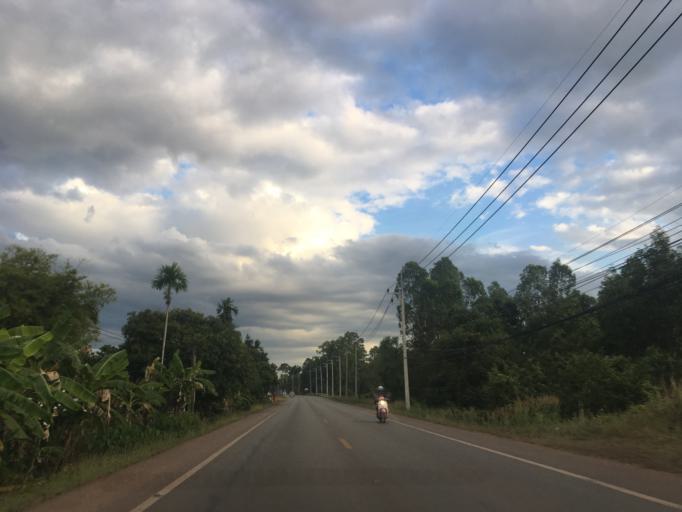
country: TH
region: Chanthaburi
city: Na Yai Am
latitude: 12.6931
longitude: 101.8074
